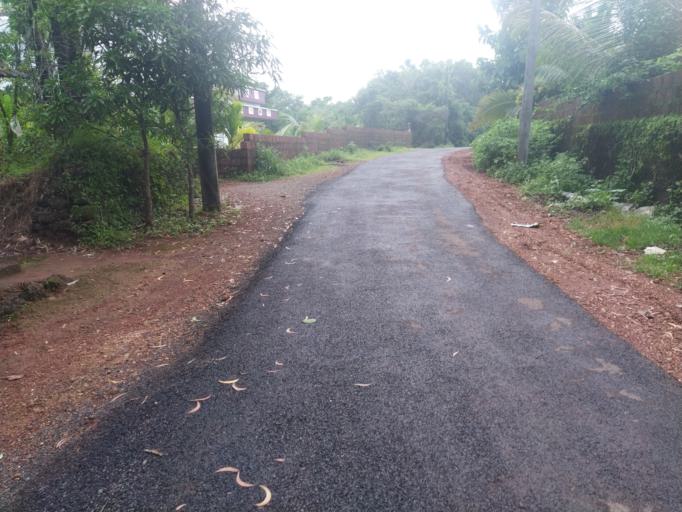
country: IN
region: Kerala
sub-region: Kasaragod District
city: Kannangad
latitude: 12.4021
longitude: 75.0587
